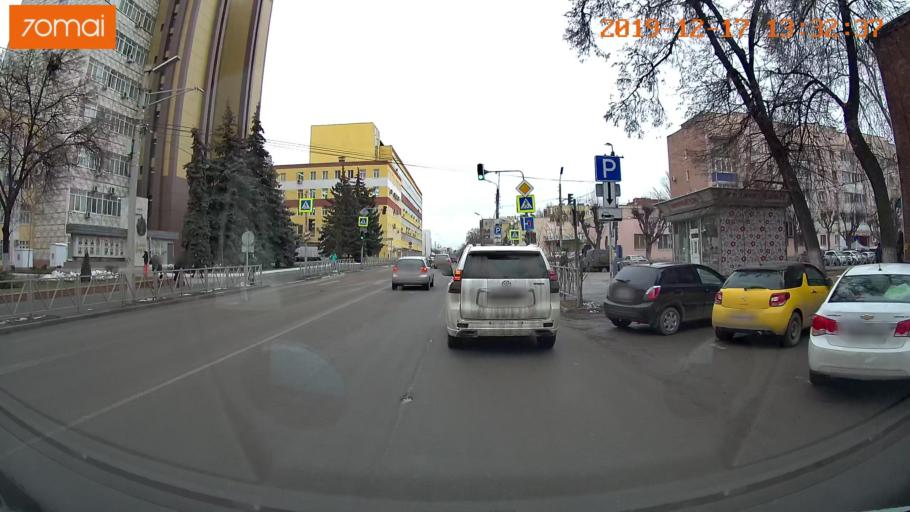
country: RU
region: Rjazan
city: Ryazan'
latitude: 54.6328
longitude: 39.7271
